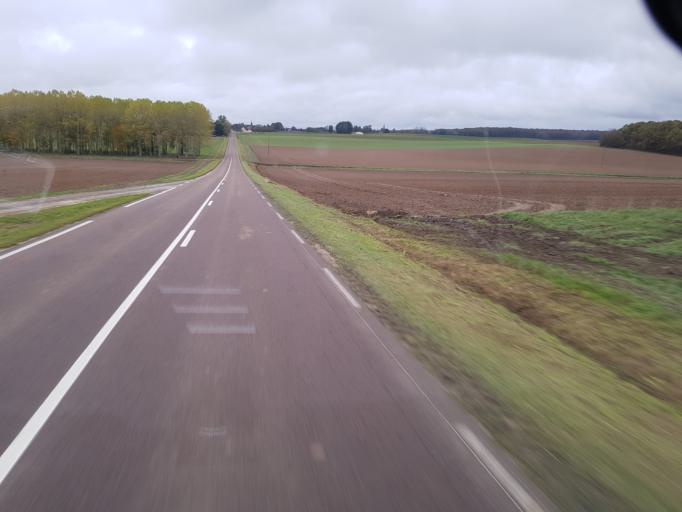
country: FR
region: Champagne-Ardenne
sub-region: Departement de la Marne
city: Esternay
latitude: 48.8060
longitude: 3.6023
